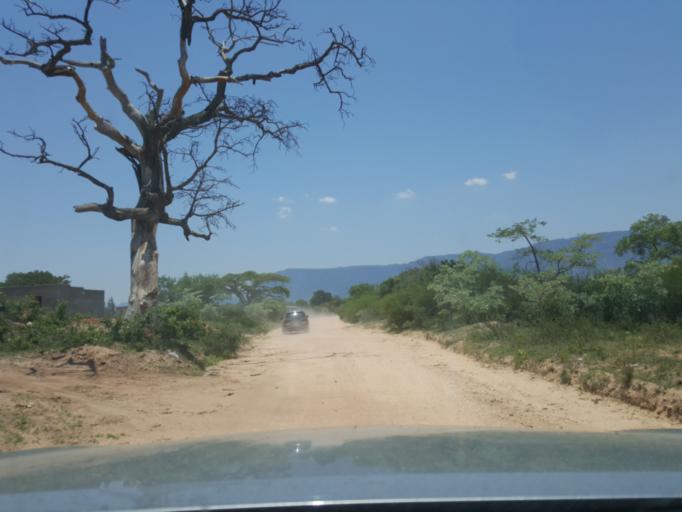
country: ZA
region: Limpopo
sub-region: Mopani District Municipality
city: Hoedspruit
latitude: -24.5810
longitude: 30.9902
